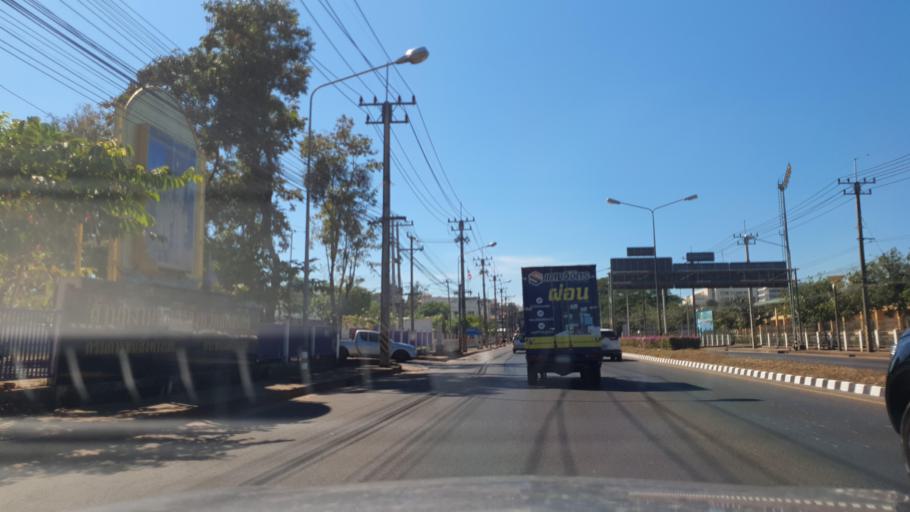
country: TH
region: Sakon Nakhon
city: Sakon Nakhon
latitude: 17.1909
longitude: 104.0949
